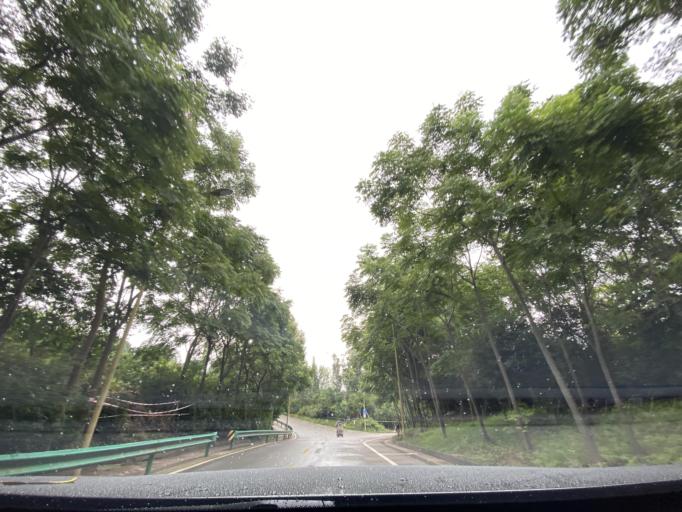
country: CN
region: Sichuan
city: Longquan
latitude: 30.6073
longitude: 104.4792
